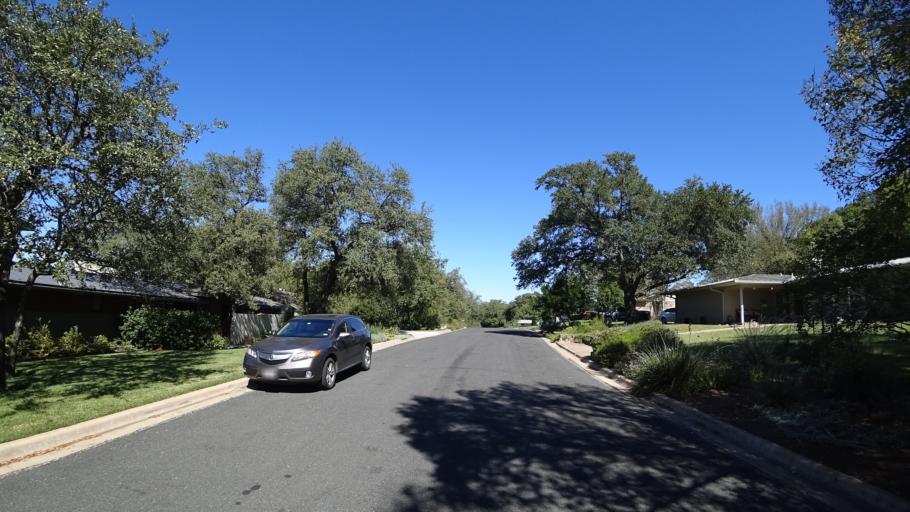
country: US
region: Texas
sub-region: Travis County
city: West Lake Hills
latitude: 30.3353
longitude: -97.7677
